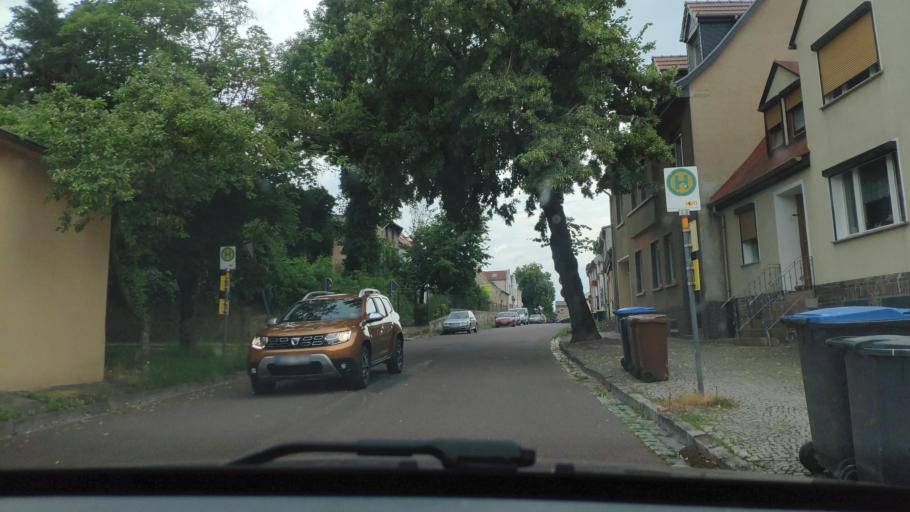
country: DE
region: Saxony-Anhalt
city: Bernburg
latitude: 51.8038
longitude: 11.7233
